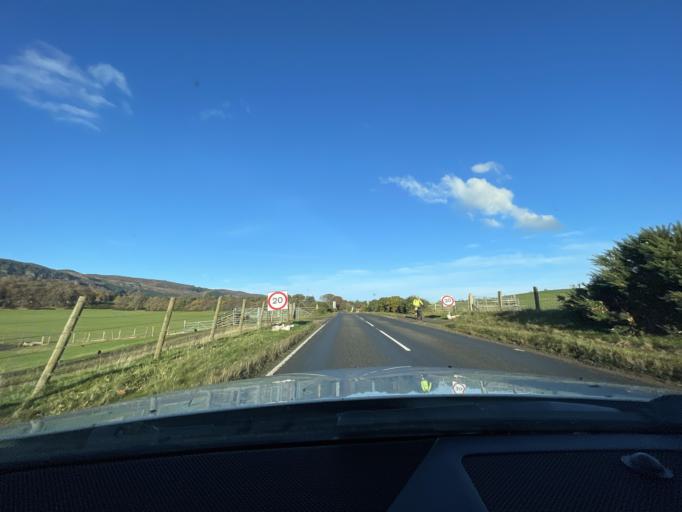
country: GB
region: Scotland
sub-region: Highland
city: Inverness
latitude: 57.3869
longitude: -4.3286
